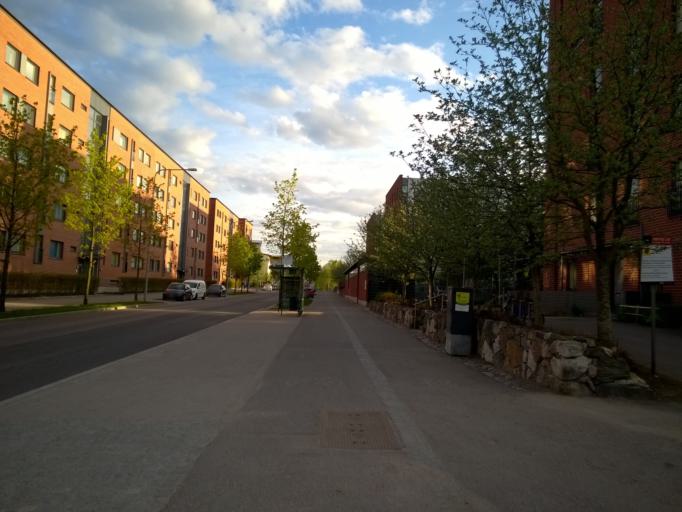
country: FI
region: Uusimaa
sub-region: Helsinki
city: Vantaa
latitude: 60.2308
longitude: 25.0300
